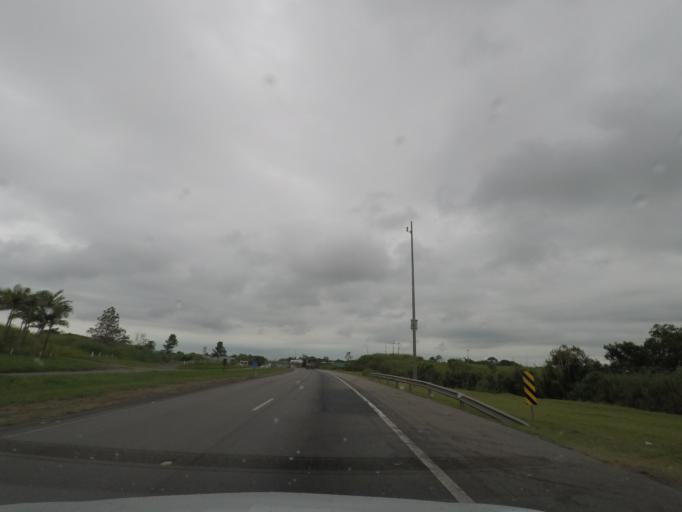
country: BR
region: Sao Paulo
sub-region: Registro
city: Registro
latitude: -24.4529
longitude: -47.8111
